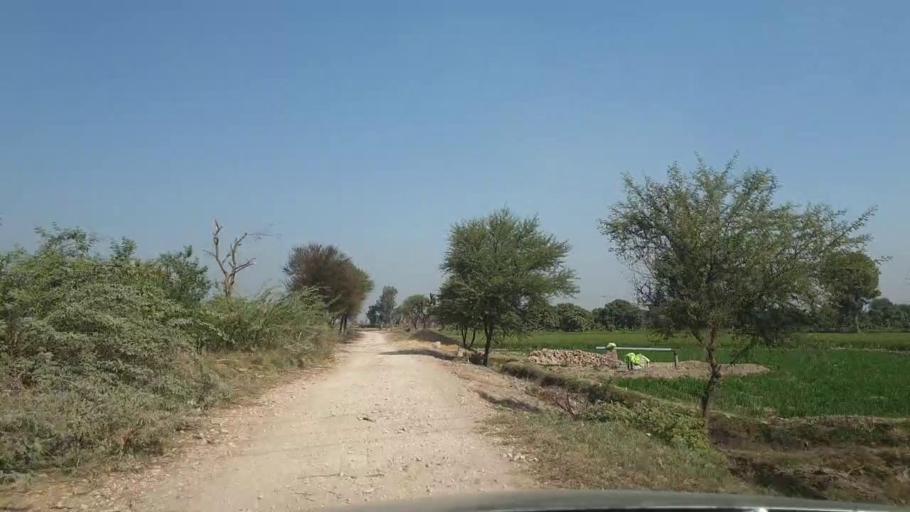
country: PK
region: Sindh
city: Tando Allahyar
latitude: 25.5891
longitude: 68.6500
